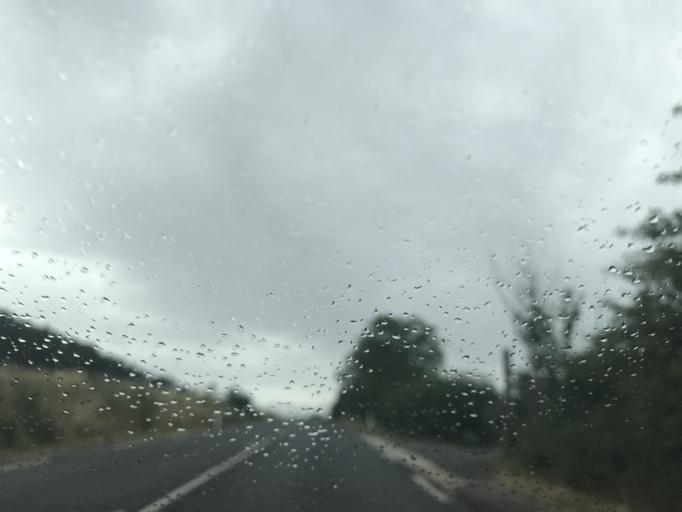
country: FR
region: Auvergne
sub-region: Departement de la Haute-Loire
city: Saint-Paulien
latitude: 45.0882
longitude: 3.8151
